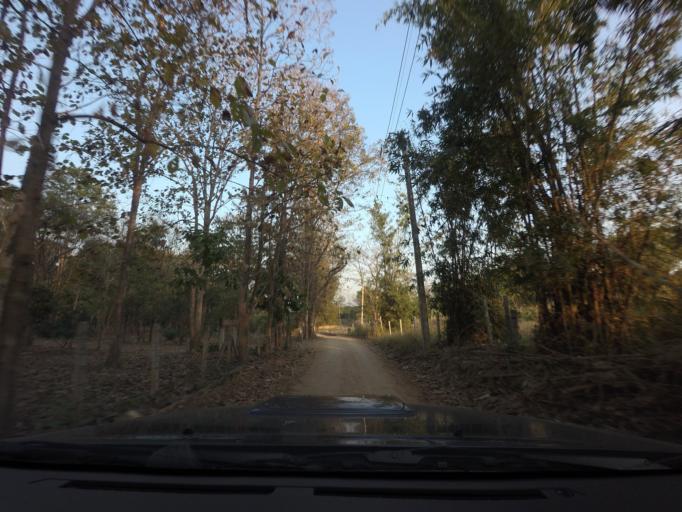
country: TH
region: Chiang Mai
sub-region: Amphoe Chiang Dao
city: Chiang Dao
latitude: 19.3663
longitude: 98.9419
